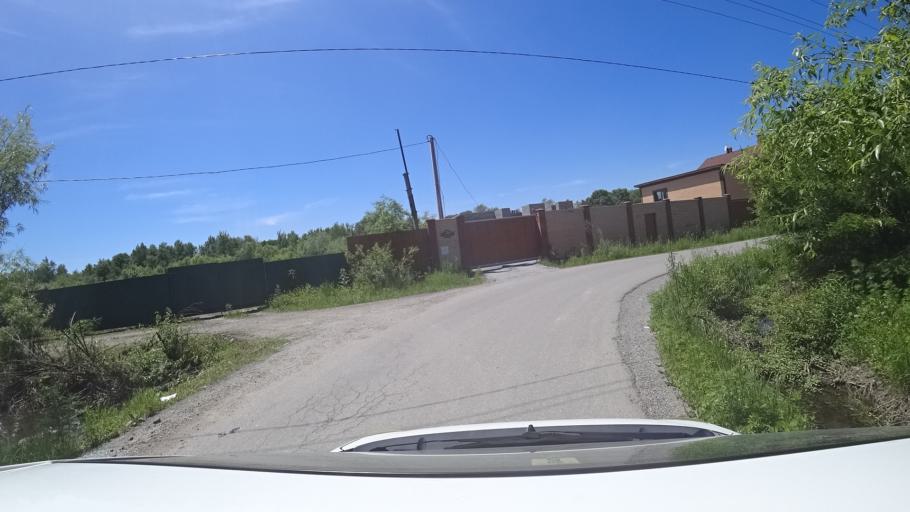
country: RU
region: Khabarovsk Krai
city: Topolevo
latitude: 48.4977
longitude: 135.1827
